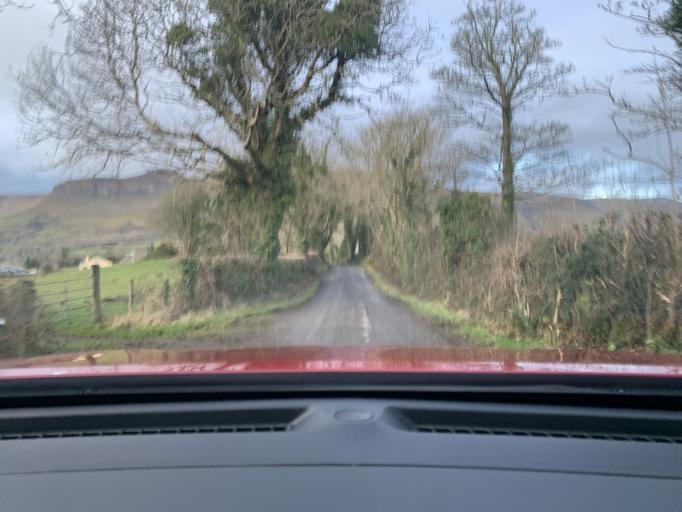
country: IE
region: Connaught
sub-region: Sligo
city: Sligo
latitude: 54.3177
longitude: -8.4483
